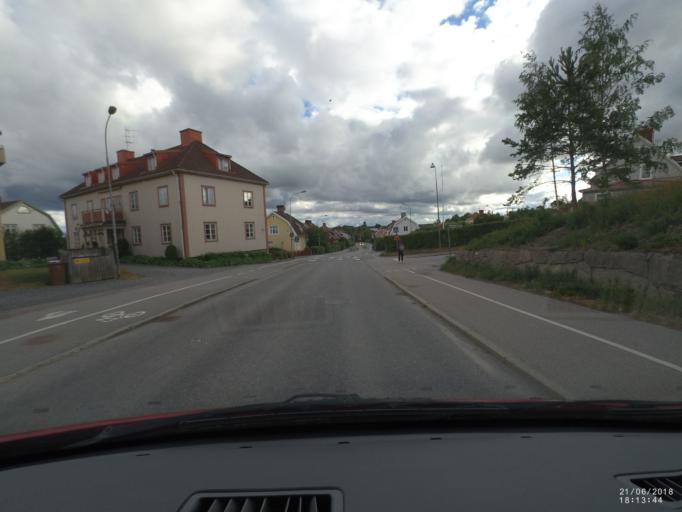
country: SE
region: Soedermanland
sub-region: Nykopings Kommun
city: Nykoping
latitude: 58.7605
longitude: 17.0195
